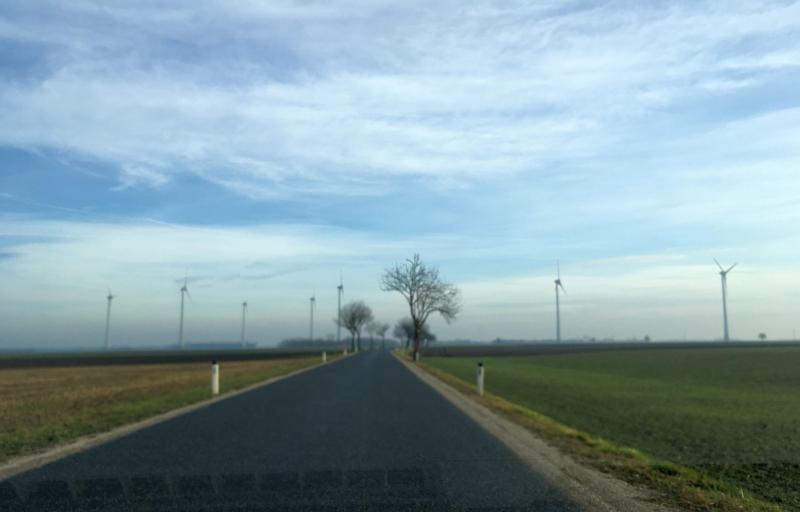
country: AT
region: Lower Austria
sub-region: Politischer Bezirk Ganserndorf
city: Andlersdorf
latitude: 48.1924
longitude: 16.6591
